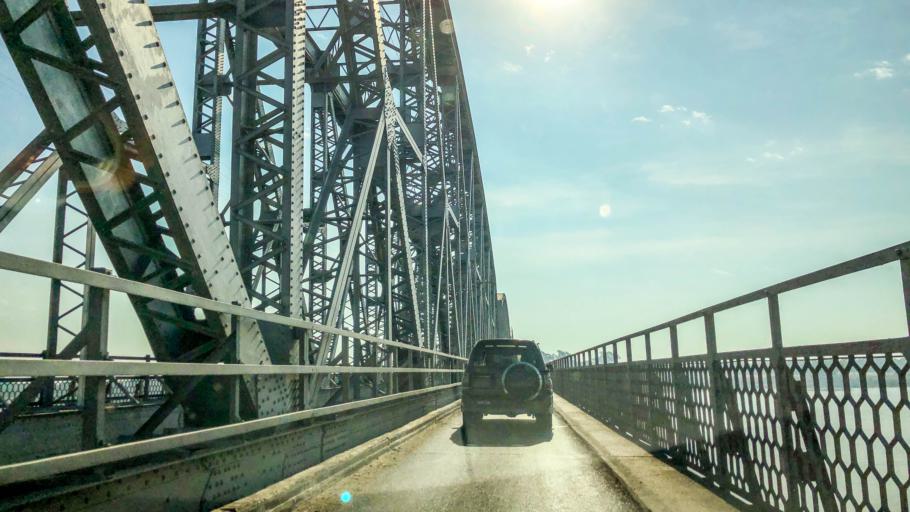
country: MM
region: Sagain
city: Sagaing
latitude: 21.8736
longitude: 95.9896
